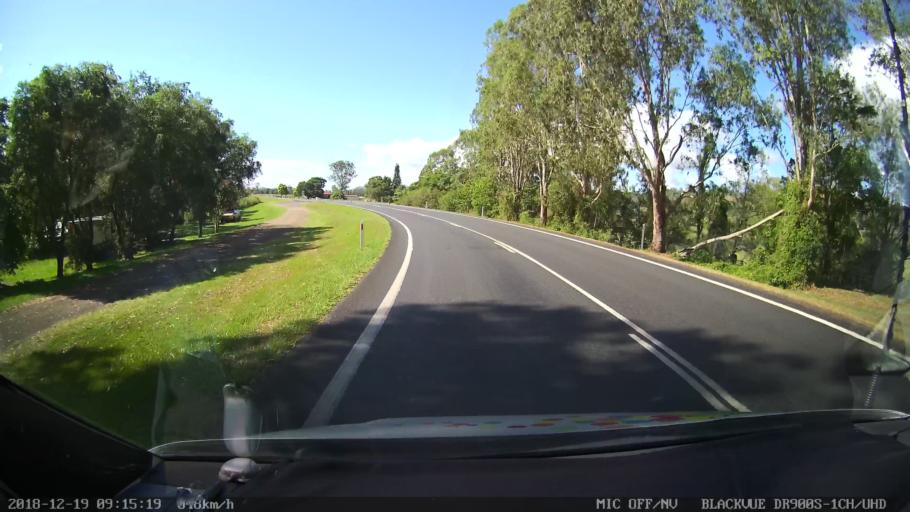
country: AU
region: New South Wales
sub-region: Kyogle
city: Kyogle
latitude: -28.5118
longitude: 152.9624
